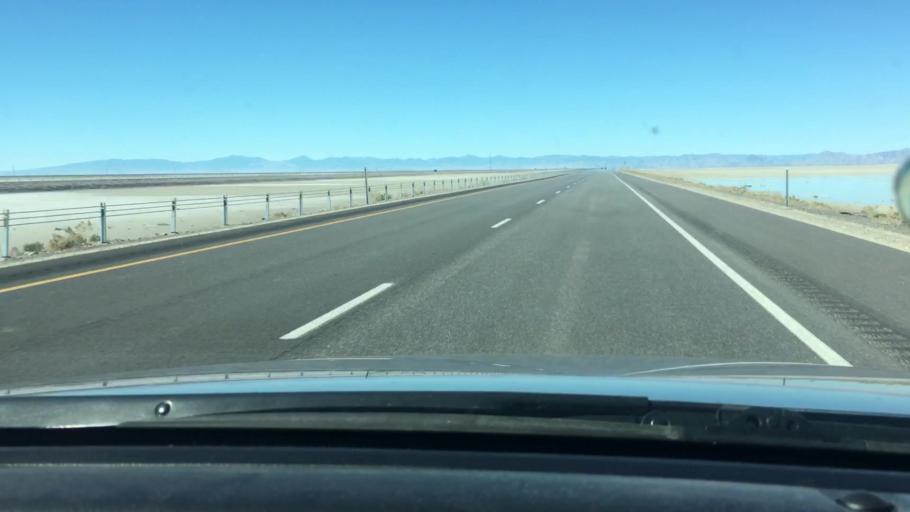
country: US
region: Utah
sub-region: Tooele County
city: Wendover
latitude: 40.7323
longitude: -113.5131
